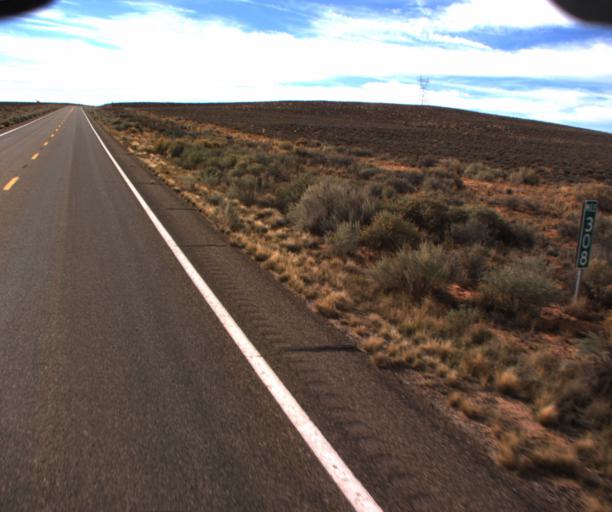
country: US
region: Arizona
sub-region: Coconino County
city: LeChee
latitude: 36.8180
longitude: -111.3071
